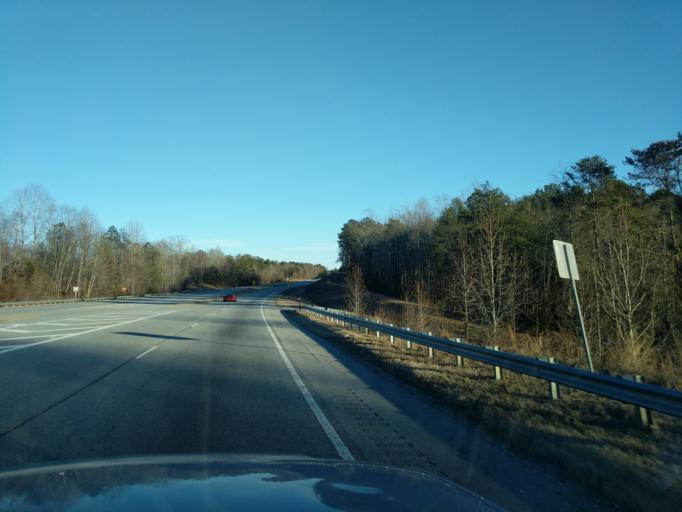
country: US
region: Georgia
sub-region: Stephens County
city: Toccoa
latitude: 34.5376
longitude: -83.3468
